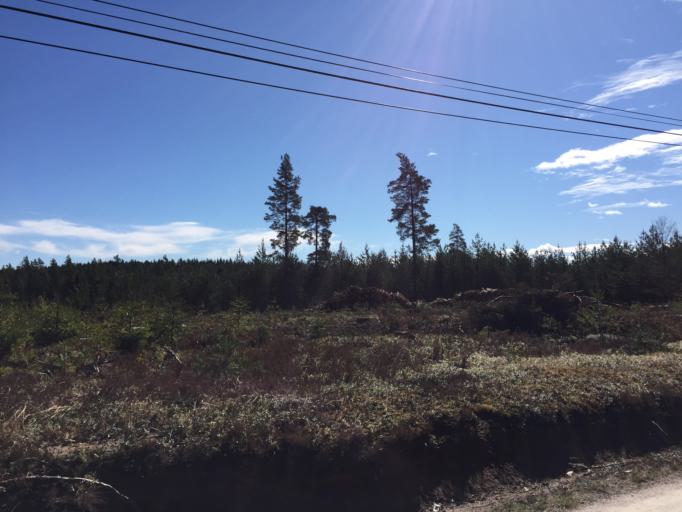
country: SE
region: Soedermanland
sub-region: Vingakers Kommun
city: Vingaker
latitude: 58.9551
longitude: 15.6711
